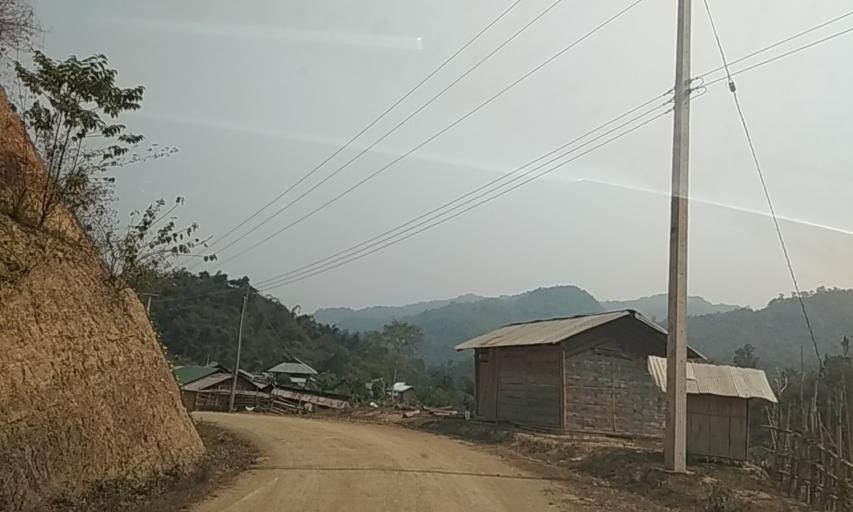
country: VN
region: Huyen Dien Bien
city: Dien Bien Phu
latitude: 21.4229
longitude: 102.7617
